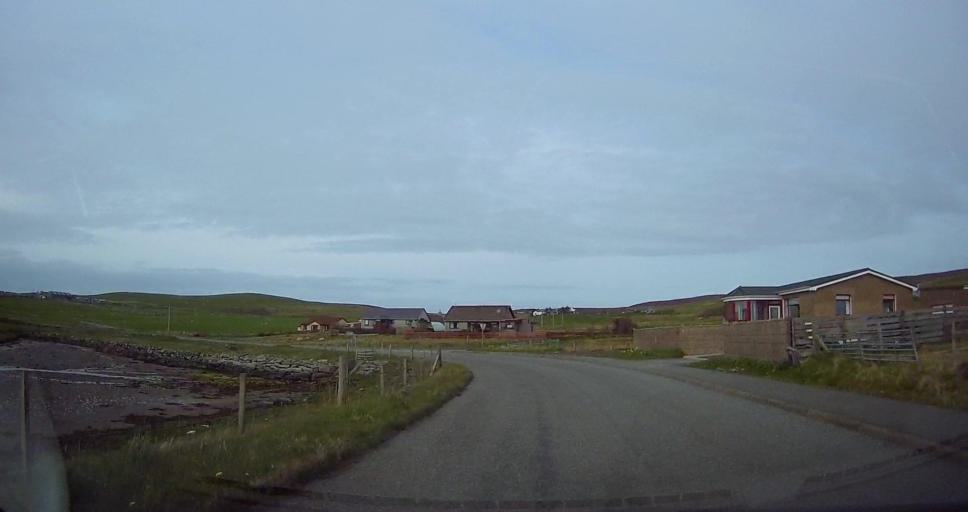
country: GB
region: Scotland
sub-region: Shetland Islands
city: Shetland
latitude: 60.1570
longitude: -1.1151
